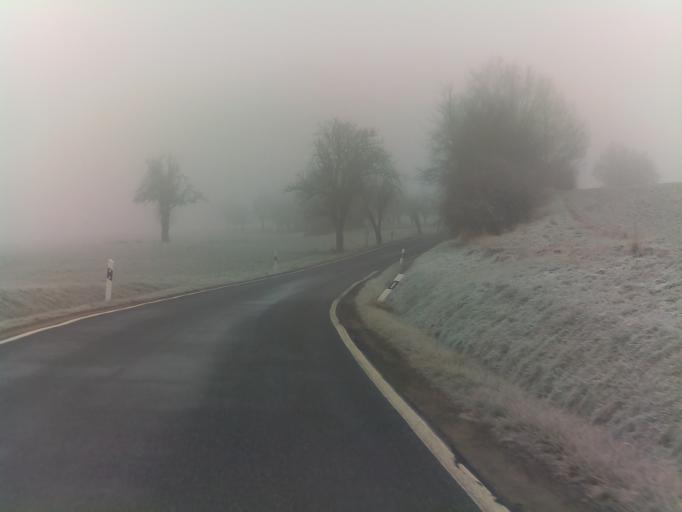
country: DE
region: Bavaria
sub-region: Regierungsbezirk Unterfranken
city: Donnersdorf
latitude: 49.9478
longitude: 10.4345
